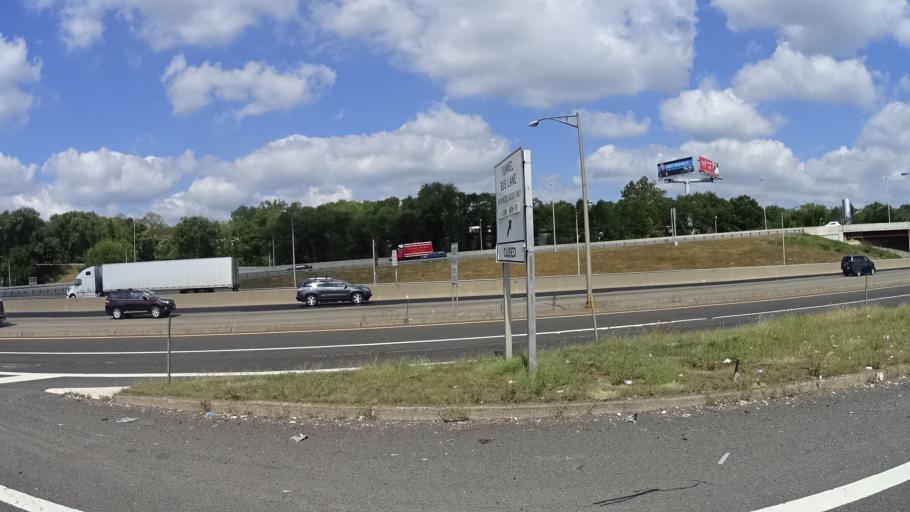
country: US
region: New Jersey
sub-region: Hudson County
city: Secaucus
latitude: 40.7795
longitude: -74.0564
